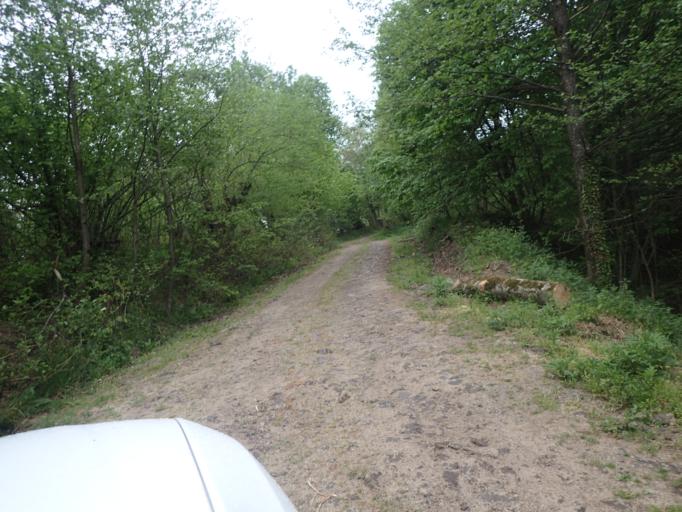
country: TR
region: Ordu
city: Akkus
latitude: 40.8703
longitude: 37.0738
